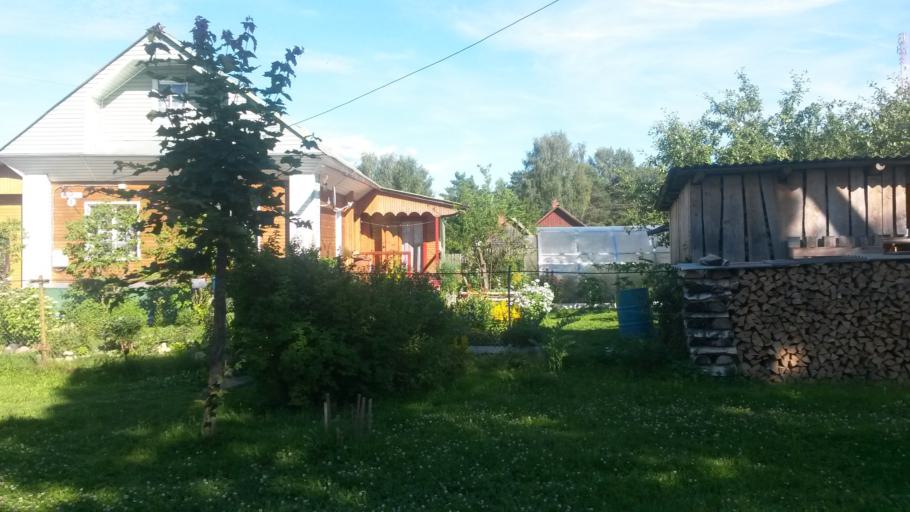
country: RU
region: Ivanovo
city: Zarechnyy
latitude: 57.4971
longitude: 42.3301
